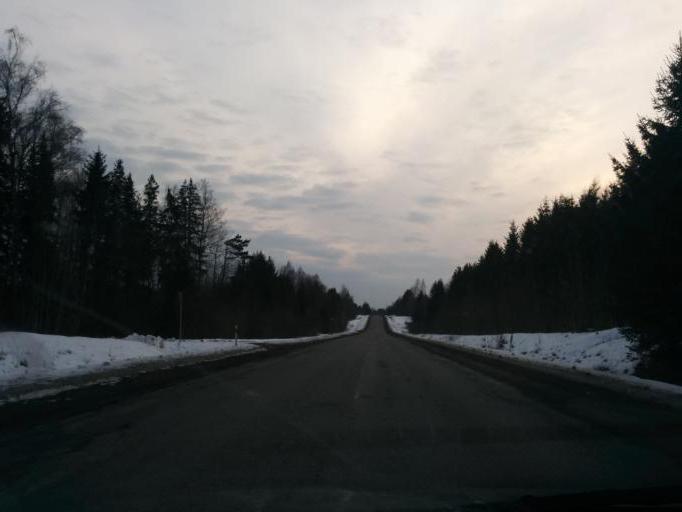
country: LV
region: Priekuli
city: Priekuli
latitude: 57.2769
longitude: 25.4829
